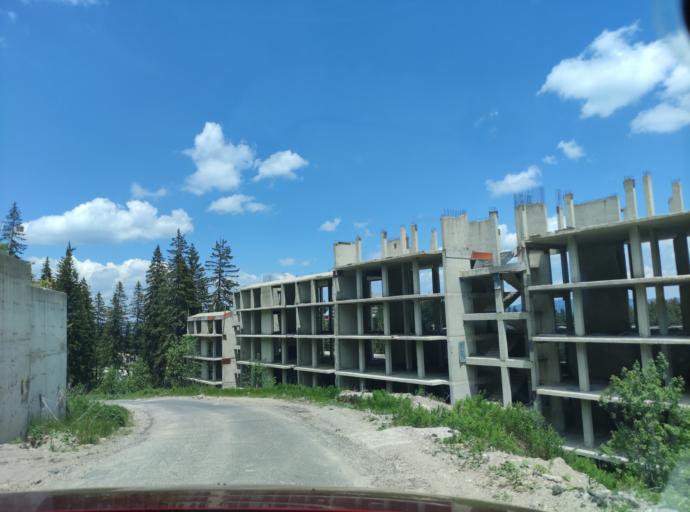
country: BG
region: Smolyan
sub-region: Obshtina Smolyan
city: Smolyan
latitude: 41.6353
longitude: 24.7003
